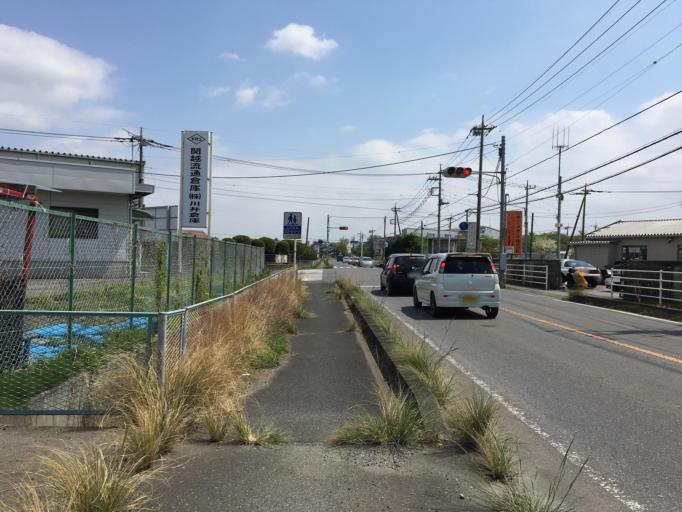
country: JP
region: Gunma
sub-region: Sawa-gun
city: Tamamura
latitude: 36.2910
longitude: 139.1466
